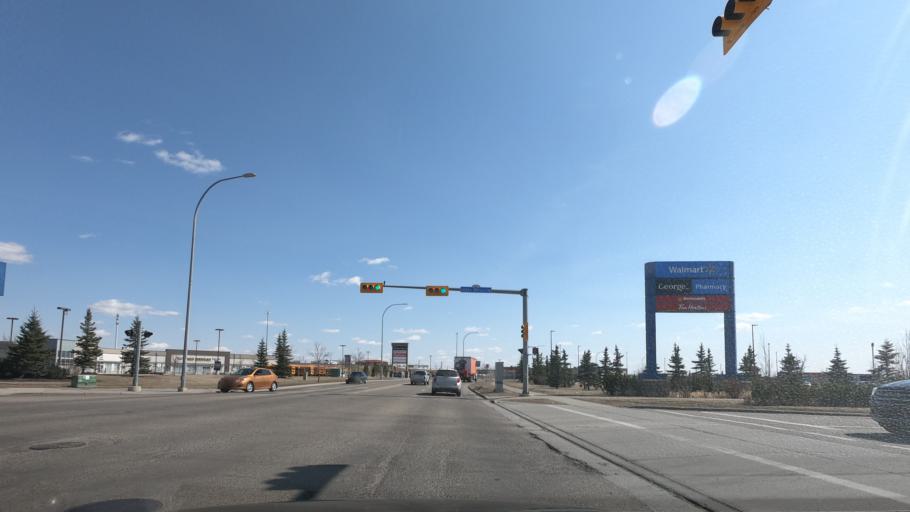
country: CA
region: Alberta
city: Airdrie
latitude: 51.2641
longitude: -114.0051
